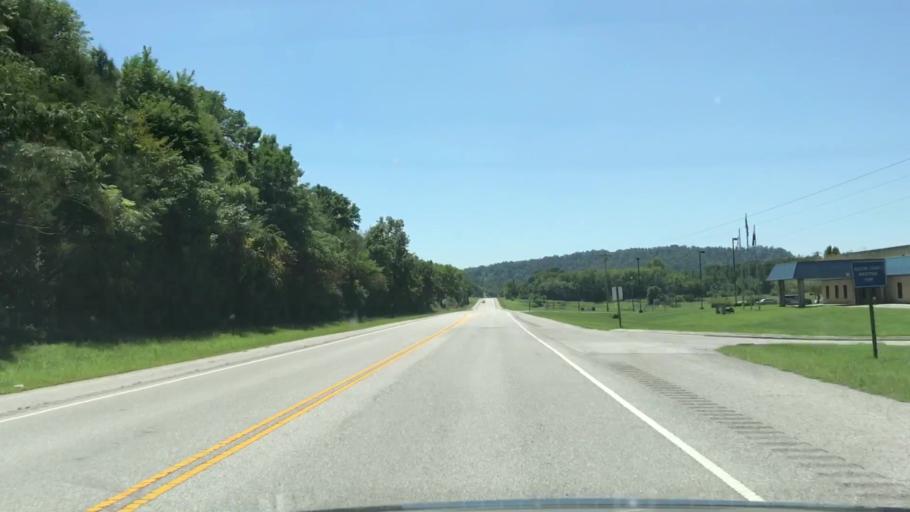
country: US
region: Tennessee
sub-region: Jackson County
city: Gainesboro
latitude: 36.3942
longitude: -85.6351
